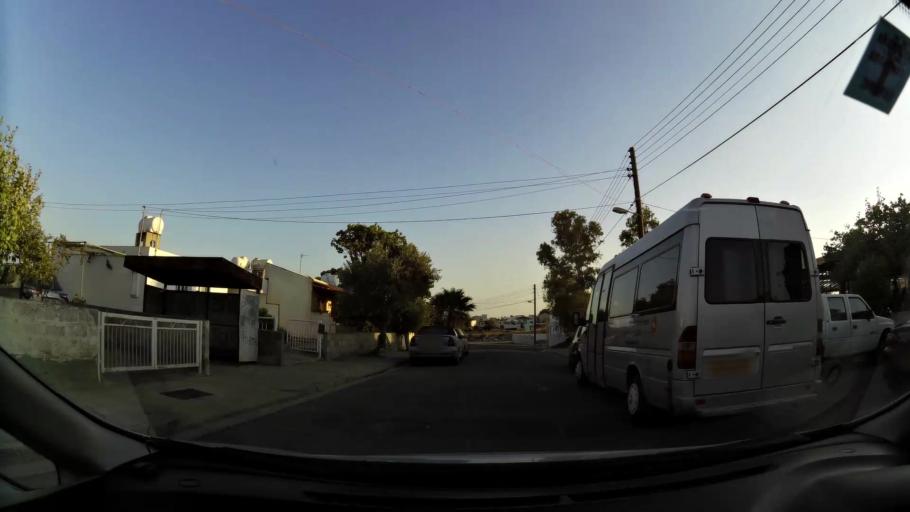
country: CY
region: Larnaka
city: Larnaca
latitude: 34.9153
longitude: 33.5917
